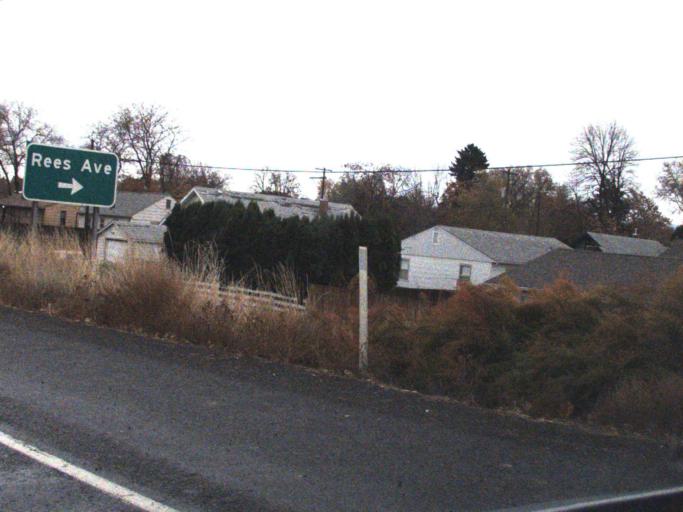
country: US
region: Washington
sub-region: Walla Walla County
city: Walla Walla
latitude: 46.0744
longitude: -118.3400
